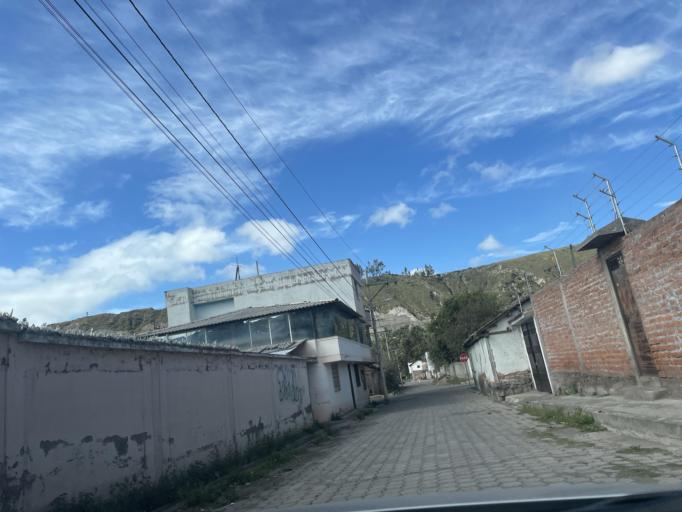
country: EC
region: Chimborazo
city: Guano
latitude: -1.6075
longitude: -78.6318
